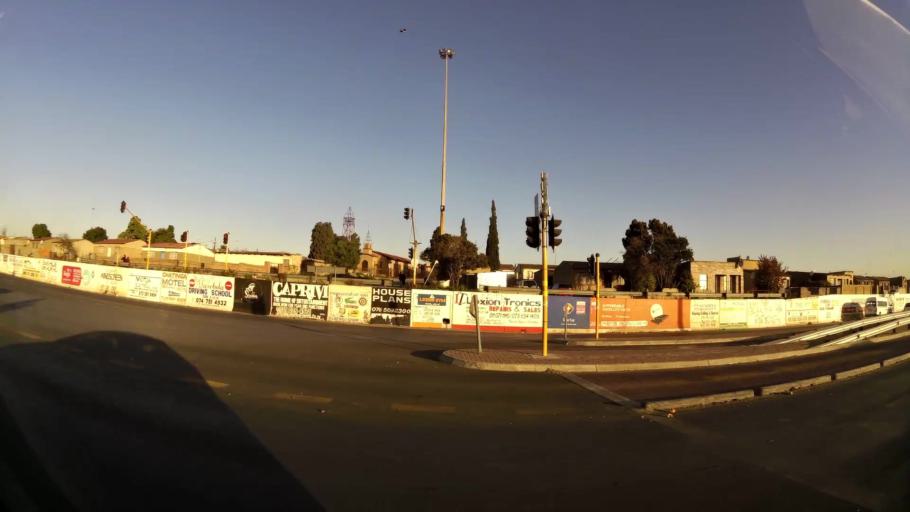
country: ZA
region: Gauteng
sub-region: Ekurhuleni Metropolitan Municipality
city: Tembisa
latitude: -26.0157
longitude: 28.2045
